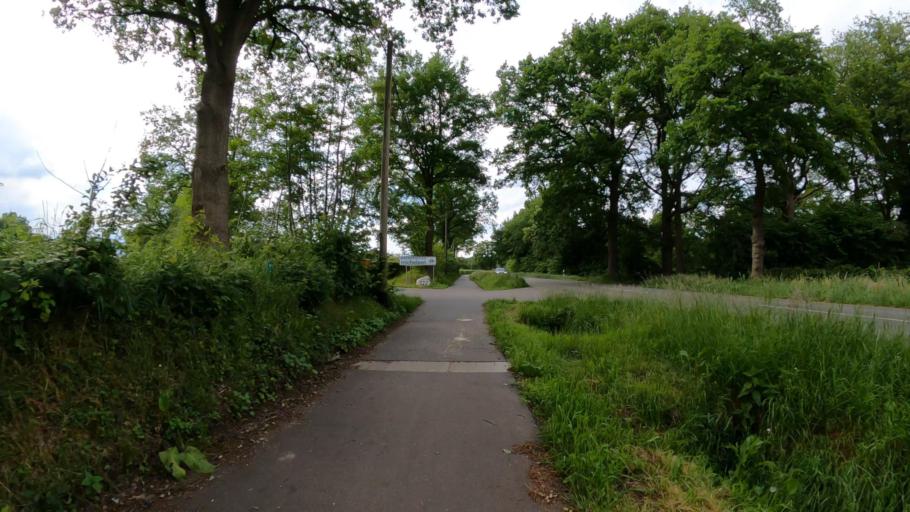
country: DE
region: Schleswig-Holstein
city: Rellingen
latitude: 53.6259
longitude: 9.7967
